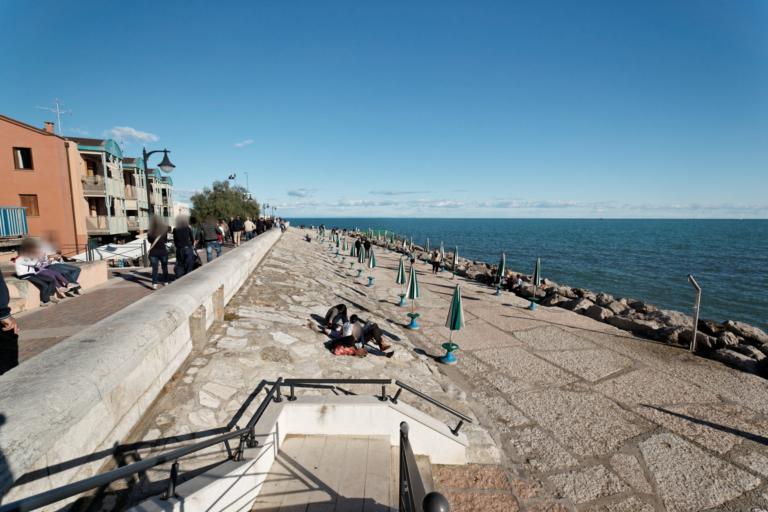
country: IT
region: Veneto
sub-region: Provincia di Venezia
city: Caorle
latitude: 45.5974
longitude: 12.8860
